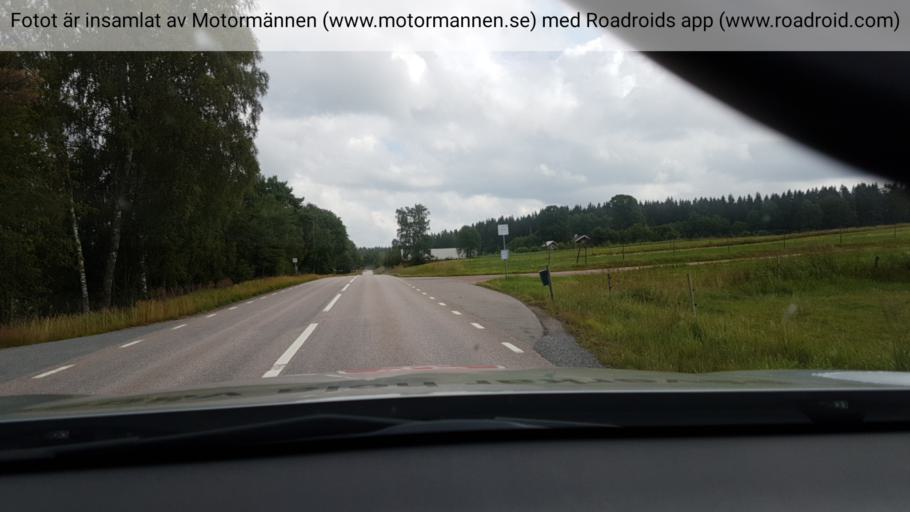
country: SE
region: Vaestra Goetaland
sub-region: Svenljunga Kommun
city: Svenljunga
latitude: 57.4823
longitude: 13.0452
